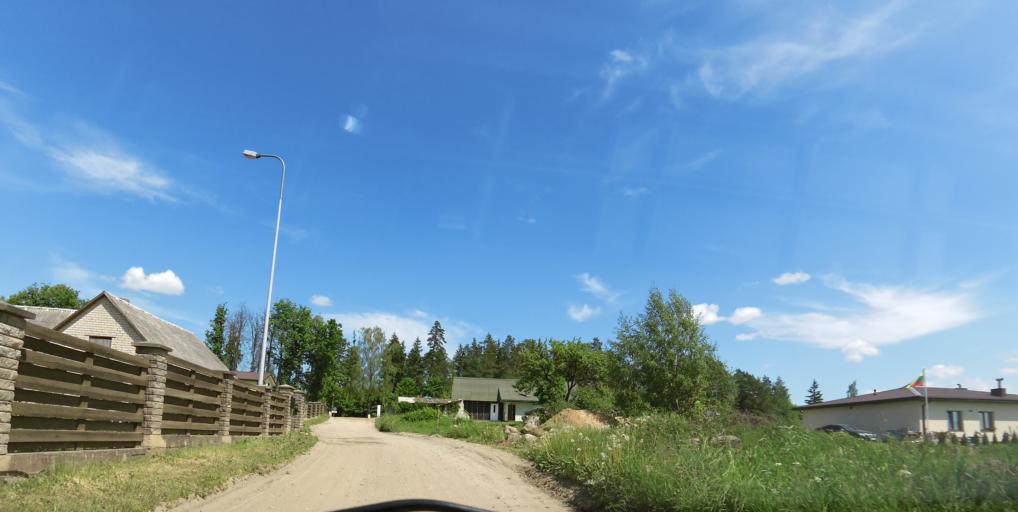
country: LT
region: Vilnius County
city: Pilaite
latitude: 54.7360
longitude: 25.1590
